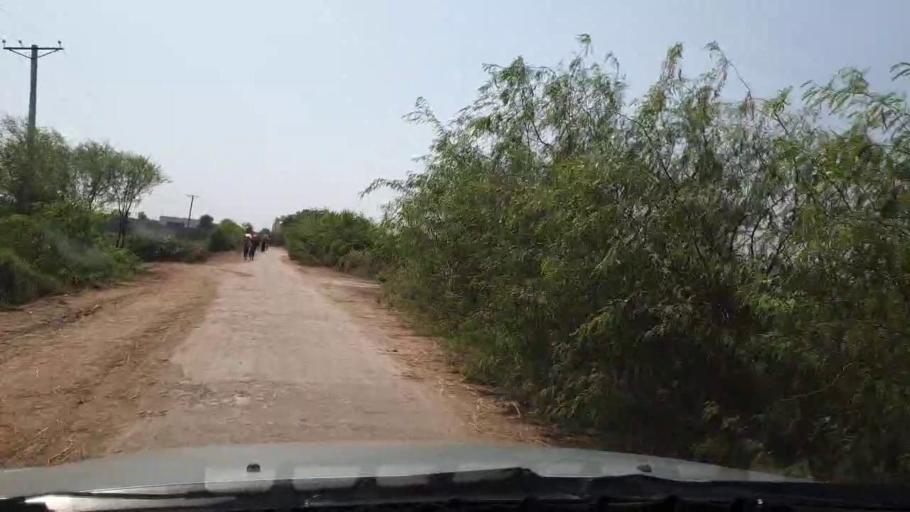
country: PK
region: Sindh
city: Tando Muhammad Khan
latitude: 25.1247
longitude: 68.6202
